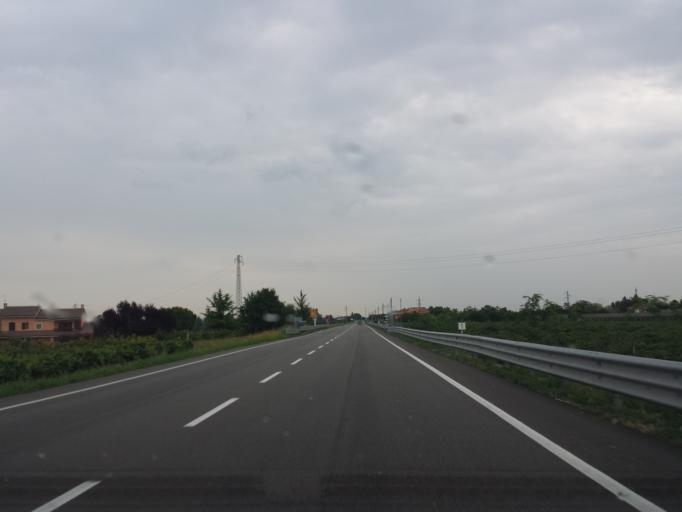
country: IT
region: Veneto
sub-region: Provincia di Verona
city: Caldierino-Rota
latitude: 45.4062
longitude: 11.1502
